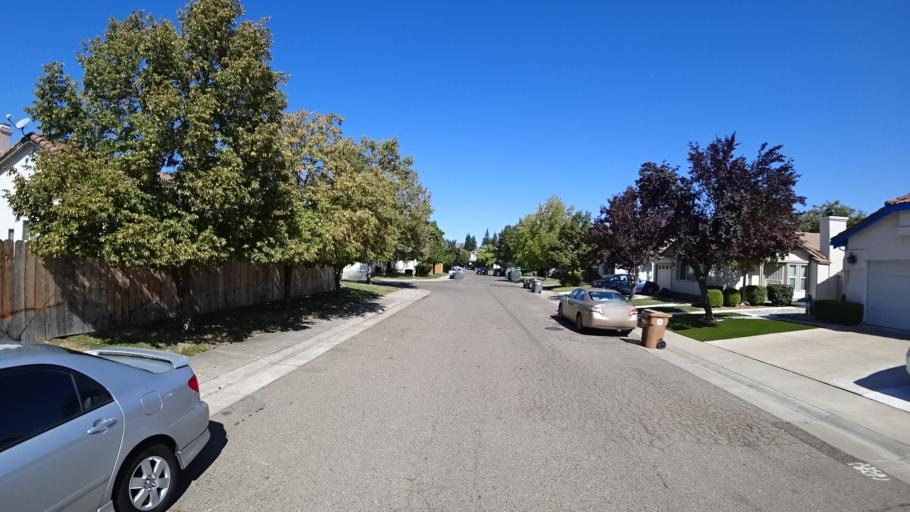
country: US
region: California
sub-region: Sacramento County
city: Laguna
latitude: 38.4244
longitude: -121.4212
